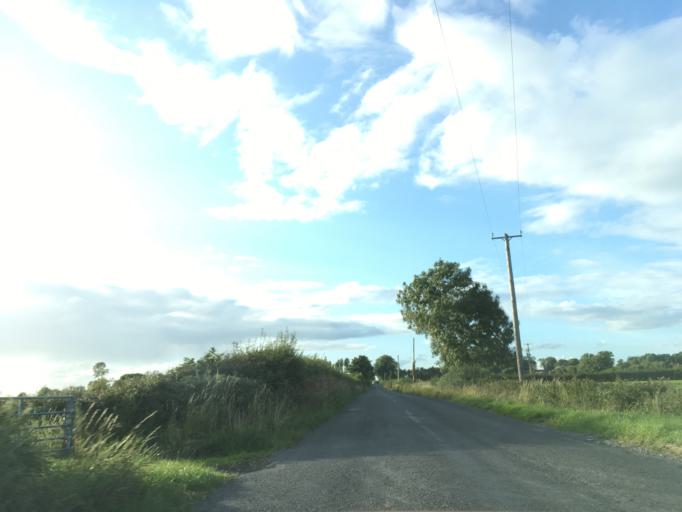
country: IE
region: Munster
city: Cashel
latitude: 52.4692
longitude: -7.9212
